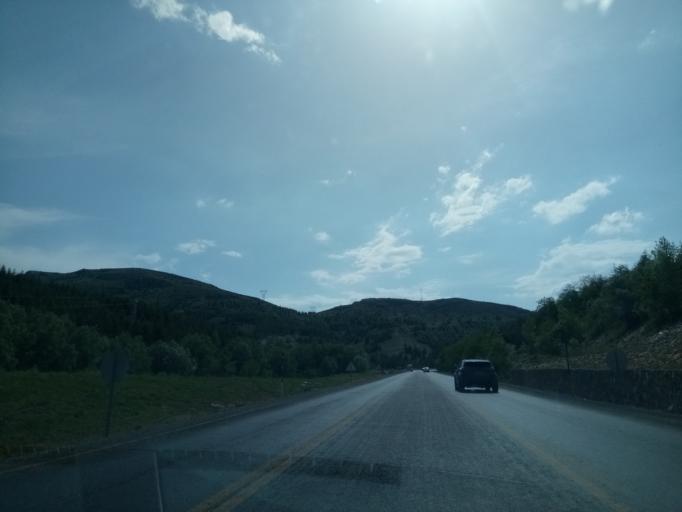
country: TR
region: Isparta
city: Bagkonak
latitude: 38.2482
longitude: 31.3584
